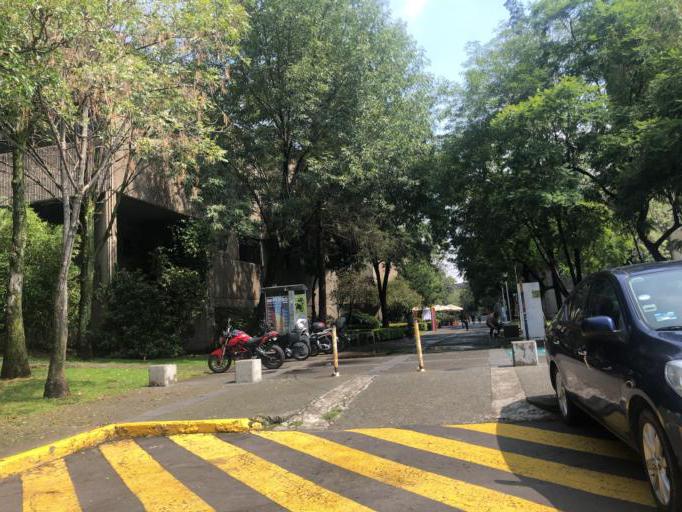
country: MX
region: Mexico City
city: Tlalpan
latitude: 19.3128
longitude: -99.1849
